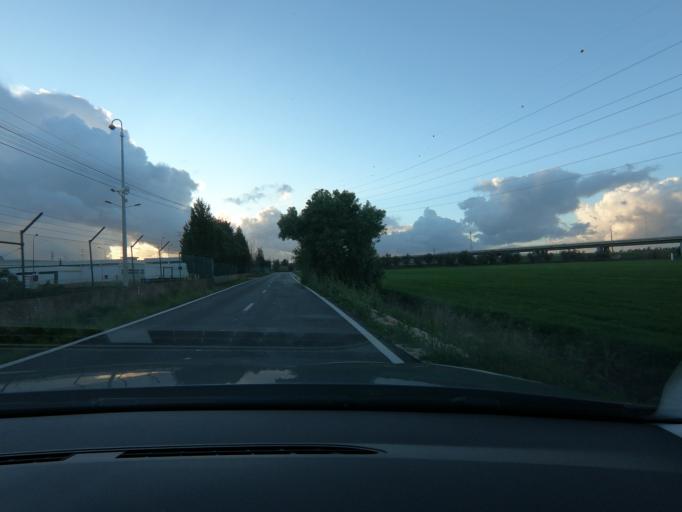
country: PT
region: Lisbon
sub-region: Alenquer
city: Carregado
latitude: 39.0148
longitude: -8.9548
